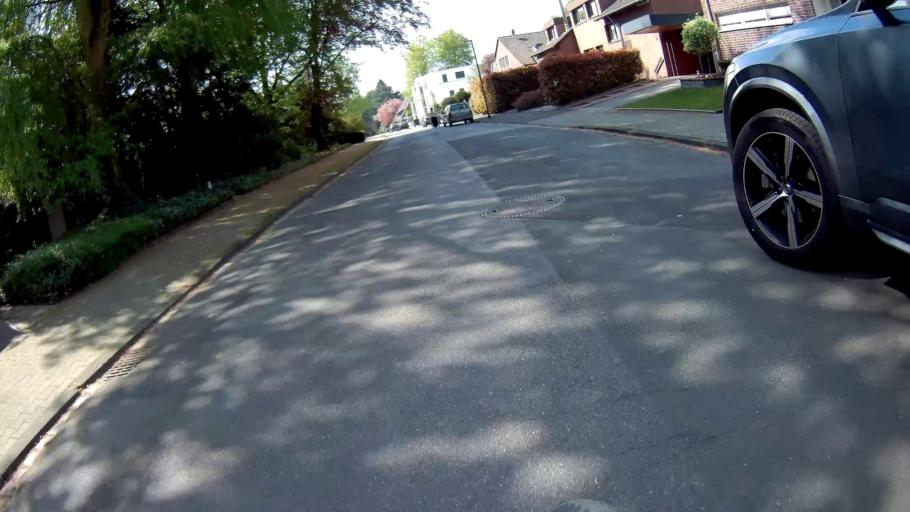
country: DE
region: North Rhine-Westphalia
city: Herten
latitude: 51.5735
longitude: 7.0706
